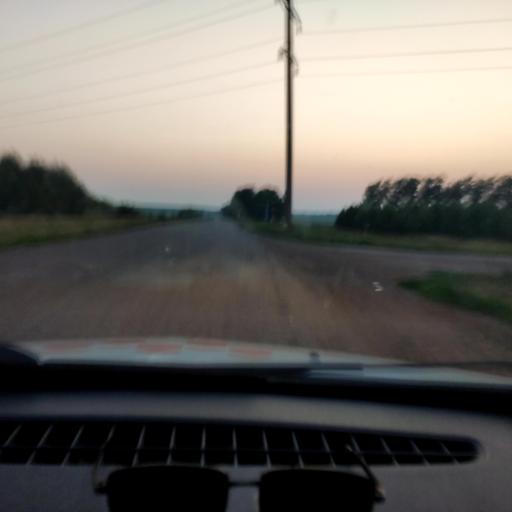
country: RU
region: Bashkortostan
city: Ulukulevo
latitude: 54.3699
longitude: 56.4252
